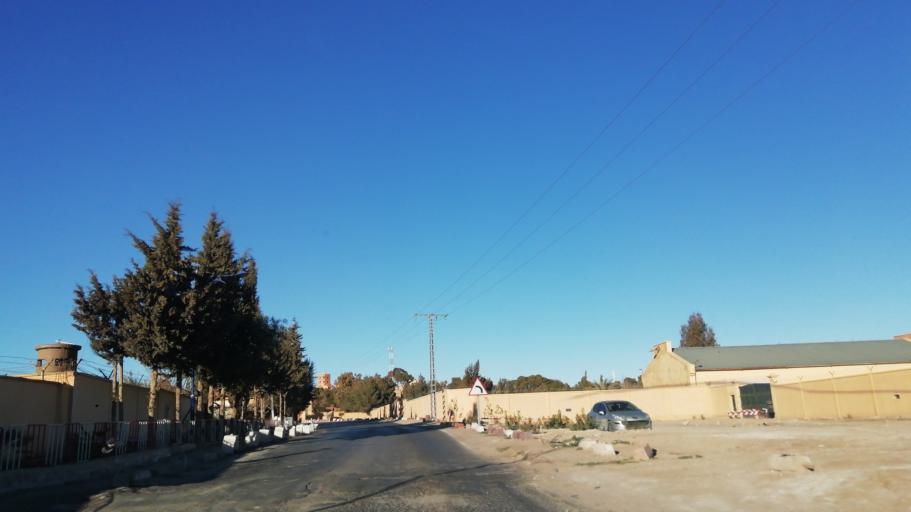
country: DZ
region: Saida
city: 'Ain el Hadjar
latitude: 34.1429
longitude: 0.0714
